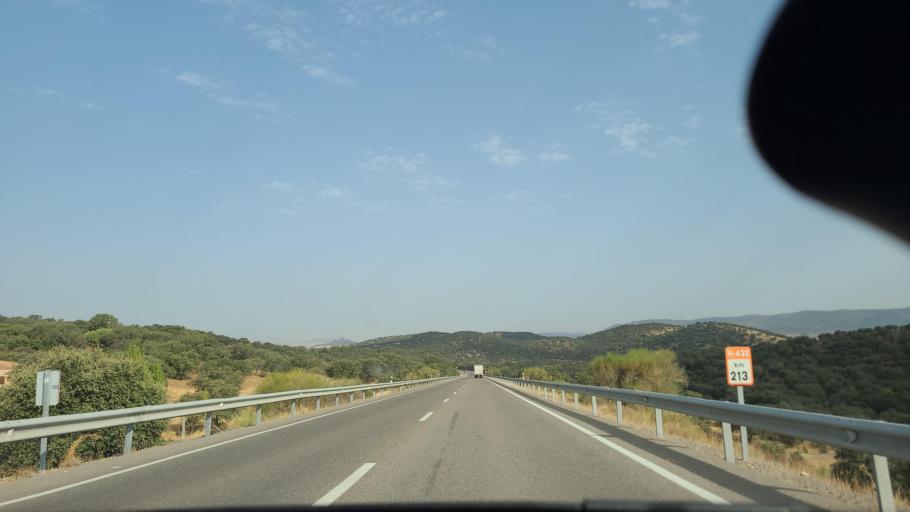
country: ES
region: Andalusia
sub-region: Province of Cordoba
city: Espiel
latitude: 38.1958
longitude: -5.0999
